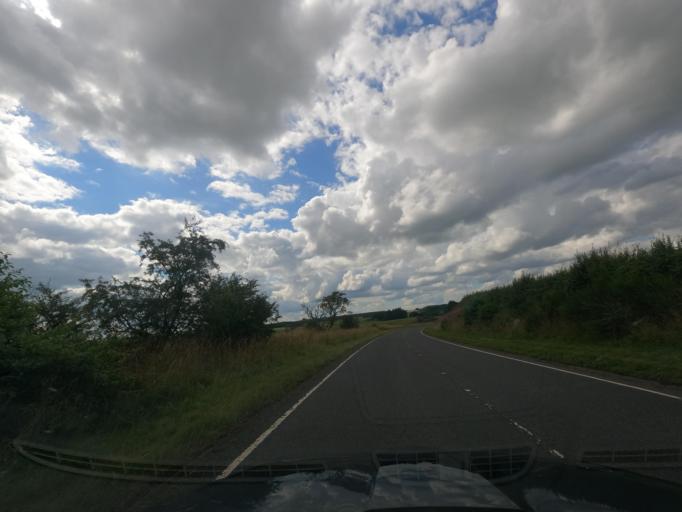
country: GB
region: Scotland
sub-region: The Scottish Borders
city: Earlston
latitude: 55.7128
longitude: -2.5422
